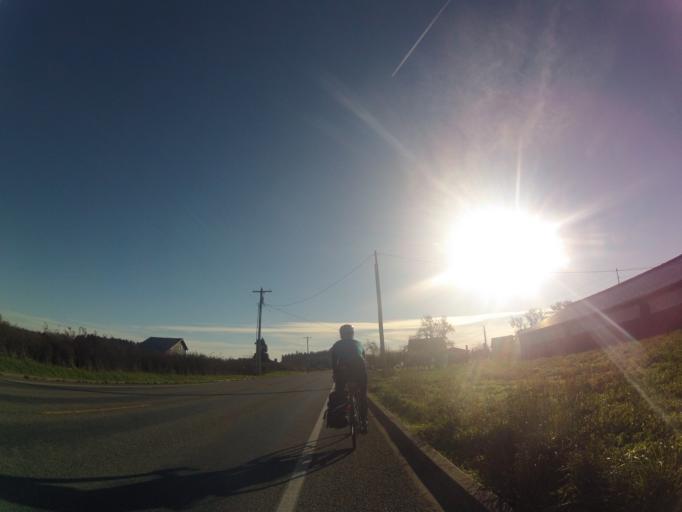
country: US
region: Washington
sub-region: Island County
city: Coupeville
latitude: 48.2001
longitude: -122.6862
